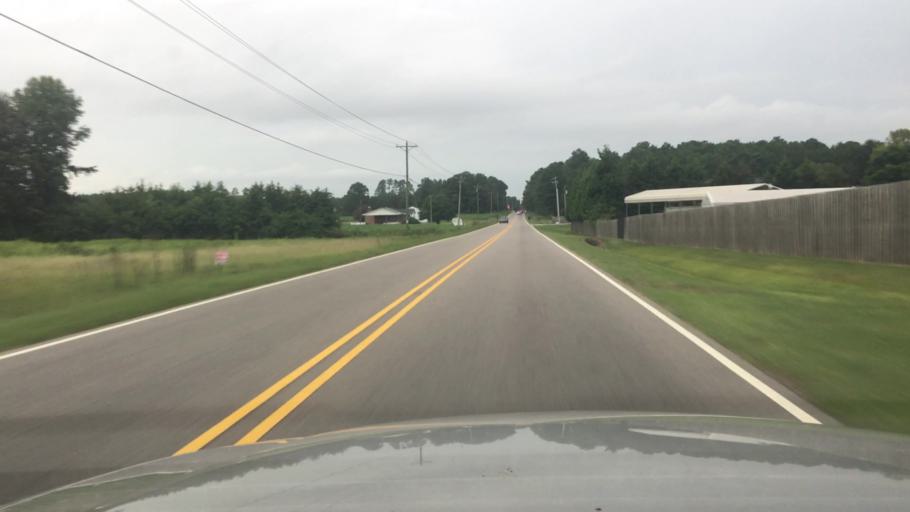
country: US
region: North Carolina
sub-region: Hoke County
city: Rockfish
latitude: 34.9715
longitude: -79.0548
